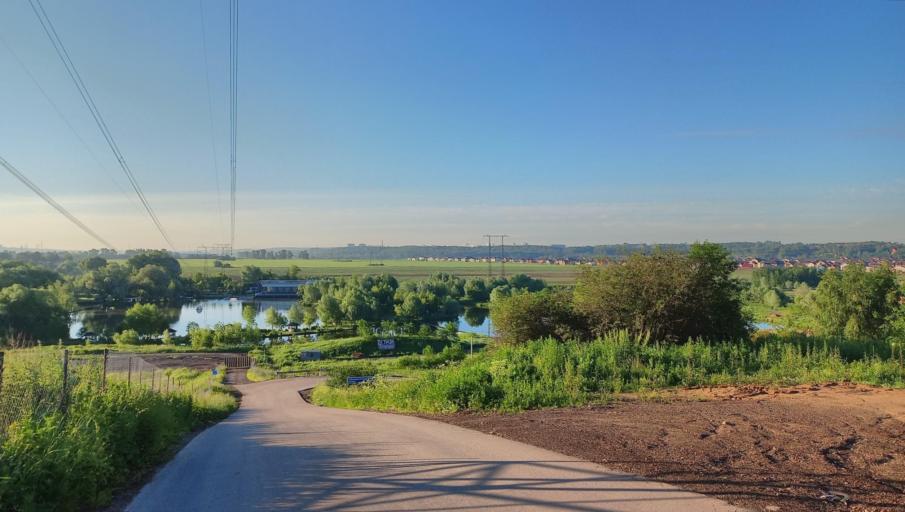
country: RU
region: Moskovskaya
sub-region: Leninskiy Rayon
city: Molokovo
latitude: 55.5844
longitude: 37.8225
